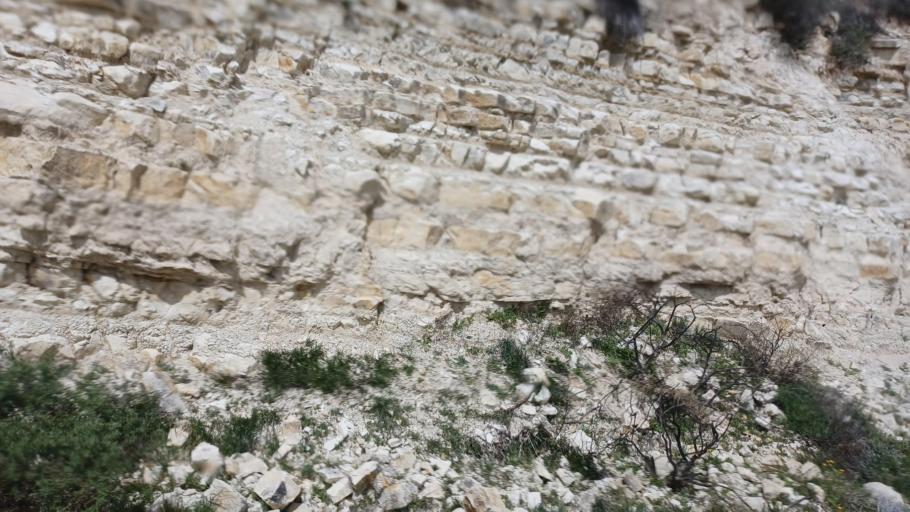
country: CY
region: Limassol
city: Pachna
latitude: 34.7733
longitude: 32.7375
